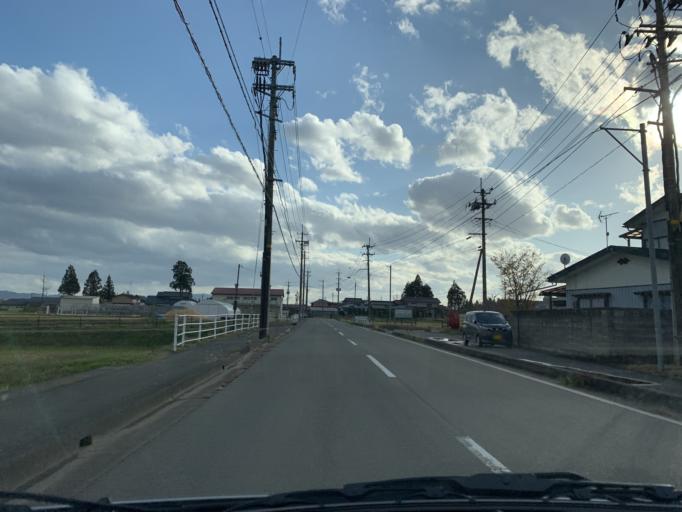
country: JP
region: Iwate
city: Mizusawa
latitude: 39.1466
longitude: 141.1590
